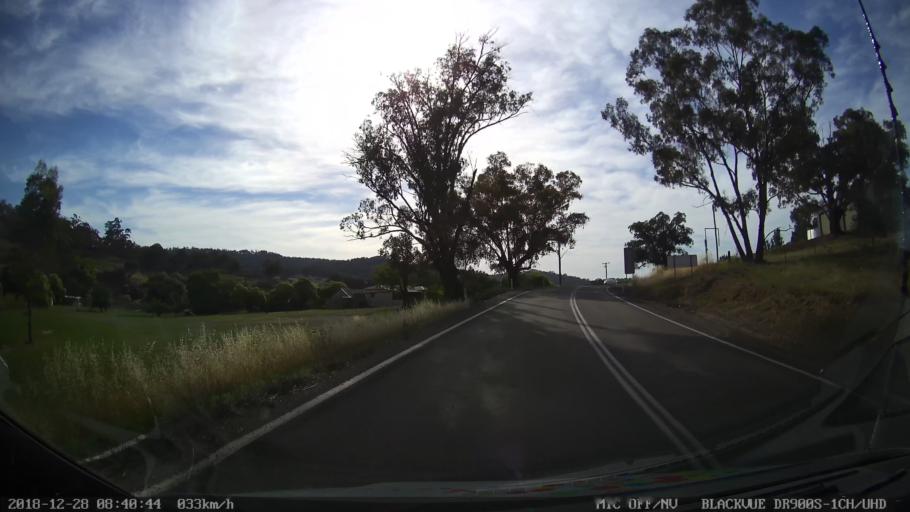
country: AU
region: New South Wales
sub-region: Upper Lachlan Shire
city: Crookwell
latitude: -34.0132
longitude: 149.3236
